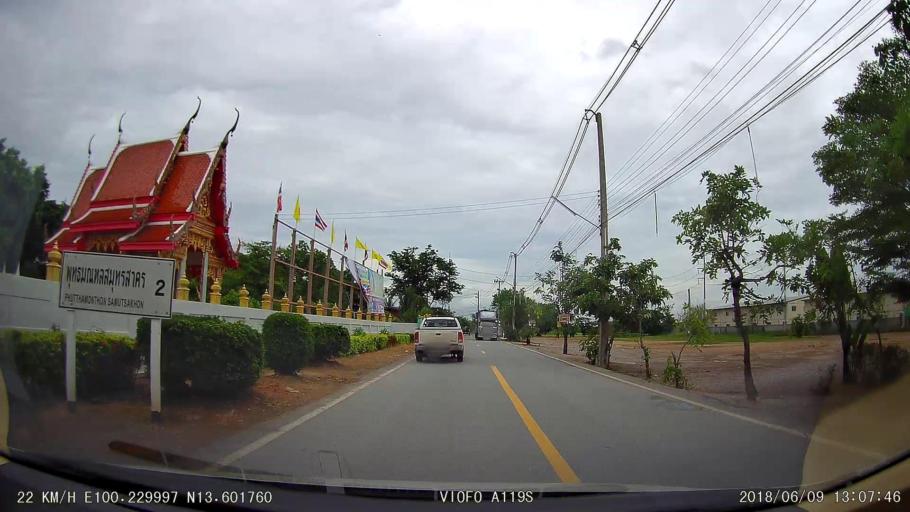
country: TH
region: Samut Sakhon
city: Krathum Baen
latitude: 13.6015
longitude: 100.2303
